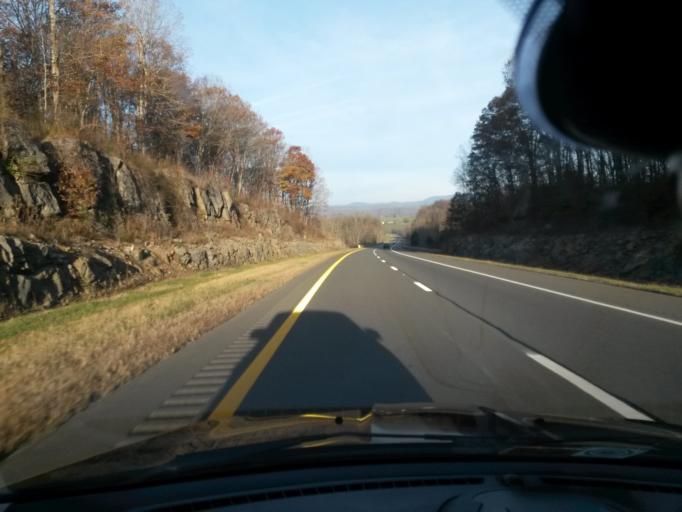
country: US
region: West Virginia
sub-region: Greenbrier County
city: Lewisburg
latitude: 37.8322
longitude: -80.4556
